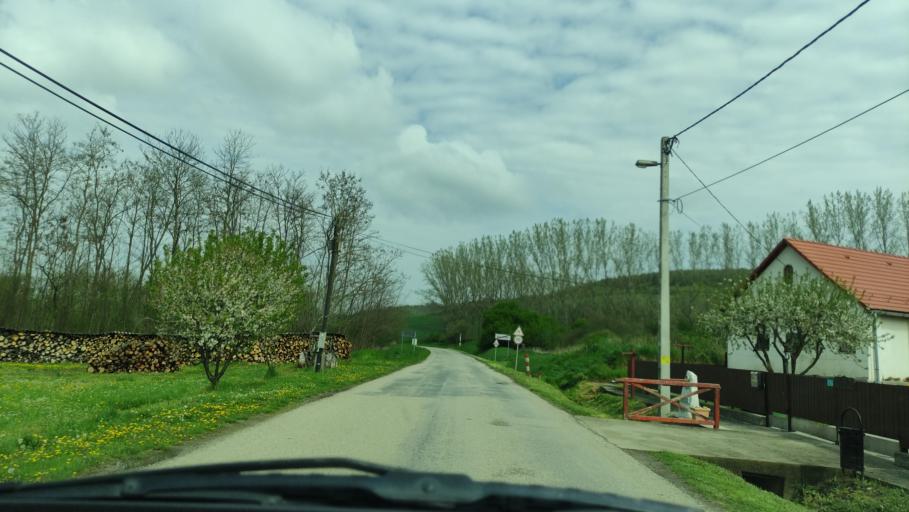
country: HU
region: Baranya
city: Magocs
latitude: 46.2809
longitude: 18.2054
